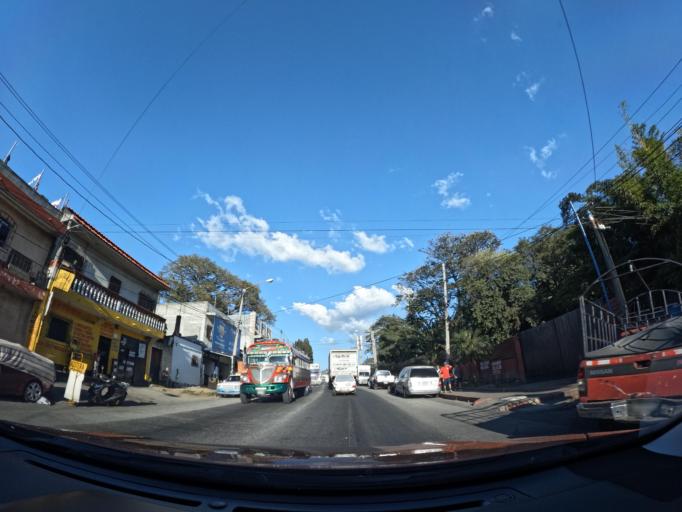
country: GT
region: Escuintla
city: Palin
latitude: 14.4044
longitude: -90.6935
